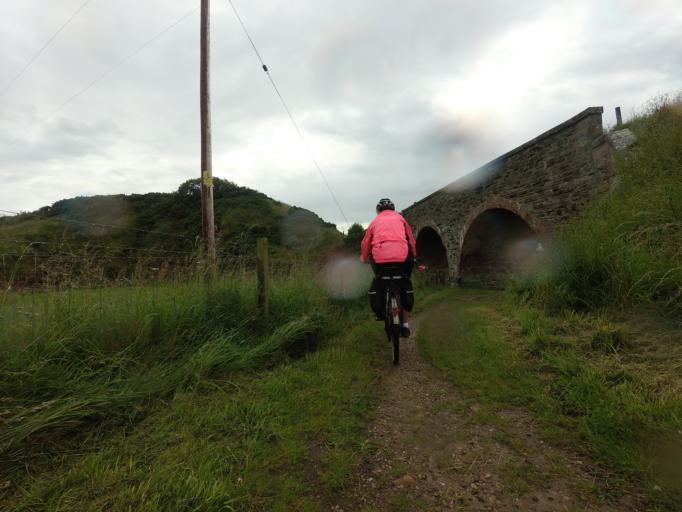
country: GB
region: Scotland
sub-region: Moray
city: Buckie
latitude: 57.6685
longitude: -2.9979
